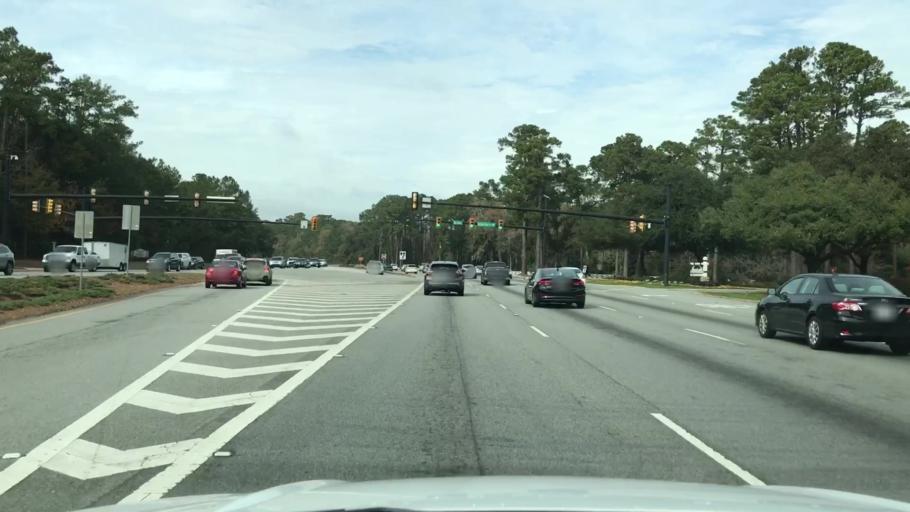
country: US
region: South Carolina
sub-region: Beaufort County
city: Bluffton
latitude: 32.2776
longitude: -80.8719
